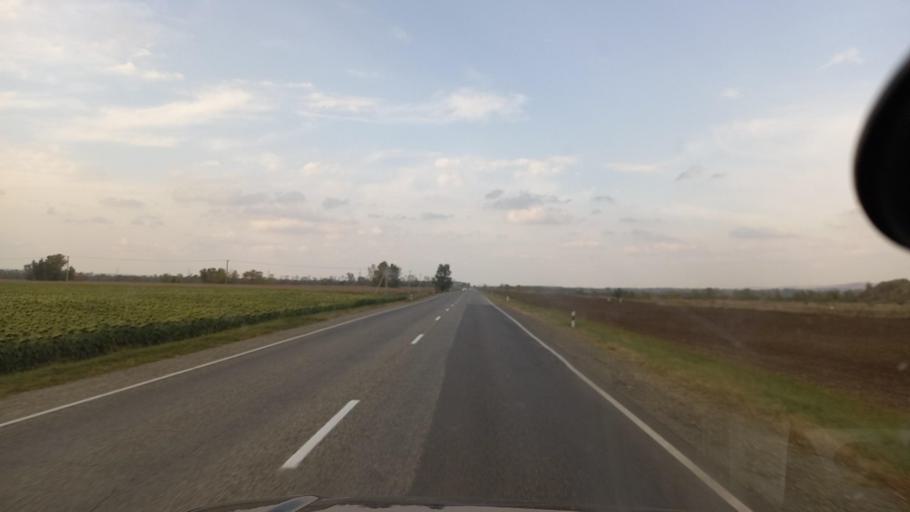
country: RU
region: Krasnodarskiy
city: Perepravnaya
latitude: 44.3588
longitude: 40.8347
